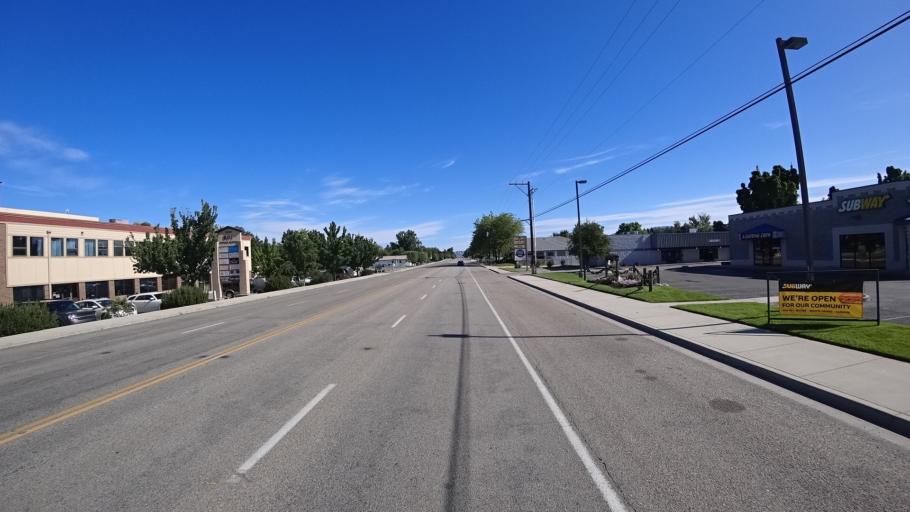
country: US
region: Idaho
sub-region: Ada County
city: Garden City
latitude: 43.5808
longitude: -116.2436
